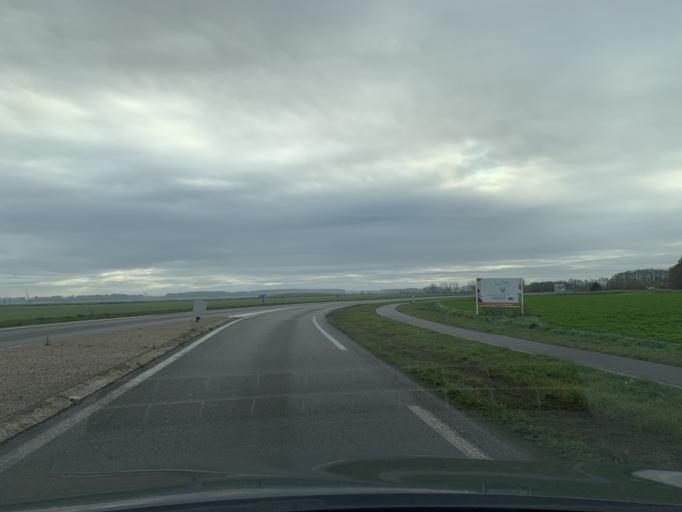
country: FR
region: Nord-Pas-de-Calais
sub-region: Departement du Nord
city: Goeulzin
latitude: 50.3296
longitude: 3.1081
